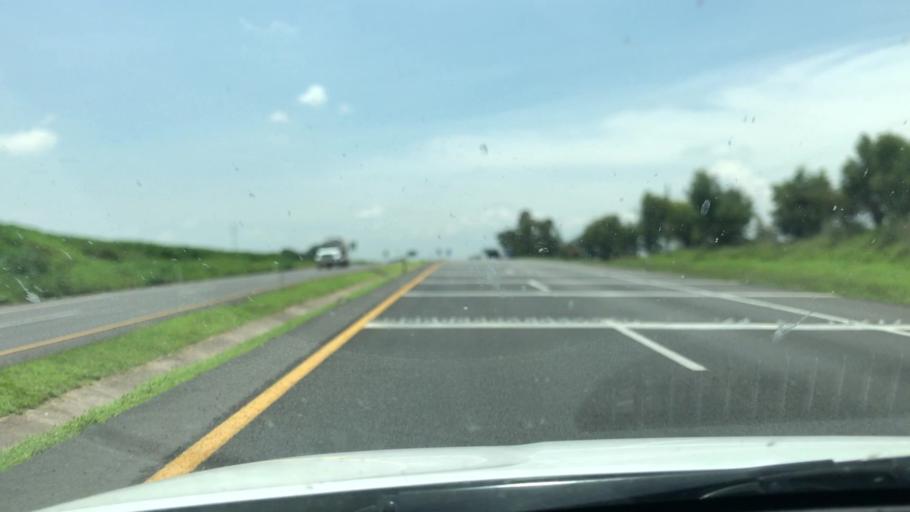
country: MX
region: Guanajuato
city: Penjamo
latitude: 20.3858
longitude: -101.7775
